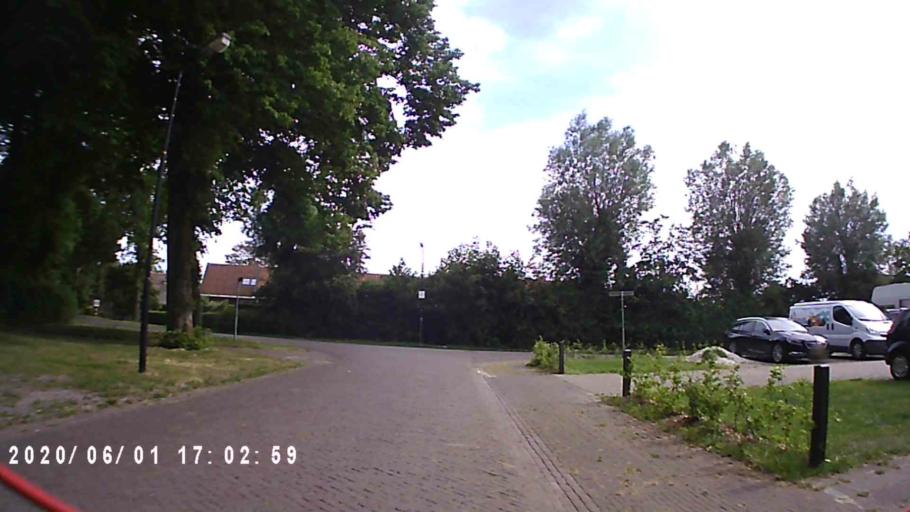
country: NL
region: Friesland
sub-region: Gemeente Tytsjerksteradiel
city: Hurdegaryp
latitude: 53.1775
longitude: 5.9290
